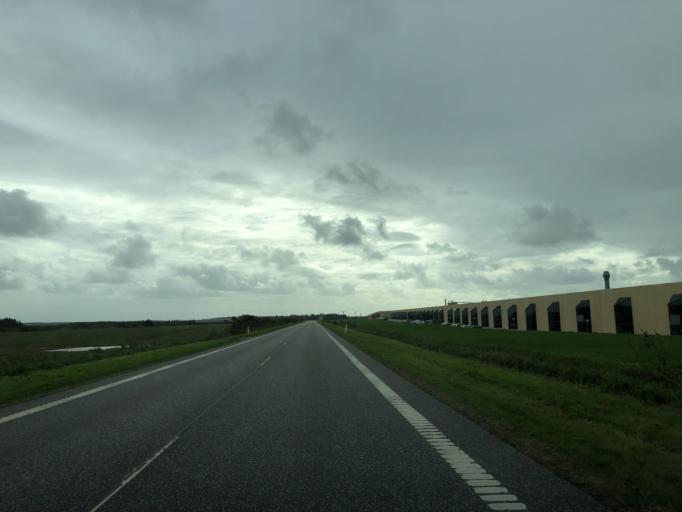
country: DK
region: North Denmark
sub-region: Thisted Kommune
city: Hurup
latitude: 56.7491
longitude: 8.4440
